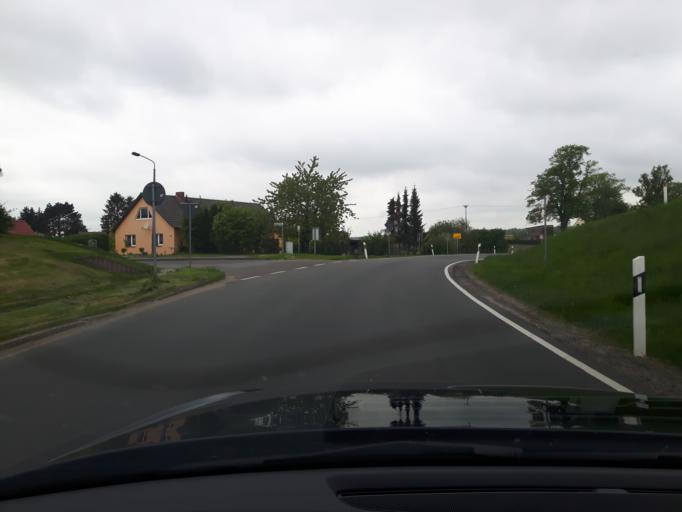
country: DE
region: Mecklenburg-Vorpommern
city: Gnoien
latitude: 54.0170
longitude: 12.6550
